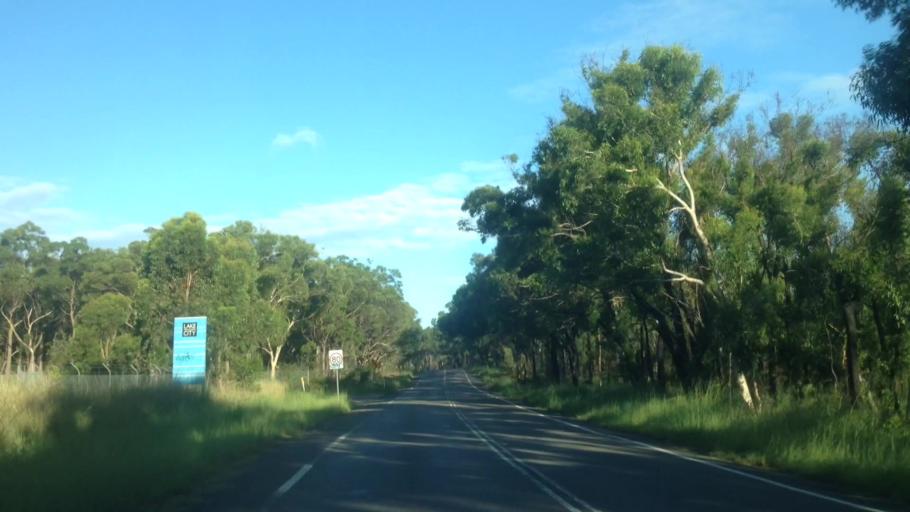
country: AU
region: New South Wales
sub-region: Wyong Shire
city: Charmhaven
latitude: -33.1934
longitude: 151.5081
